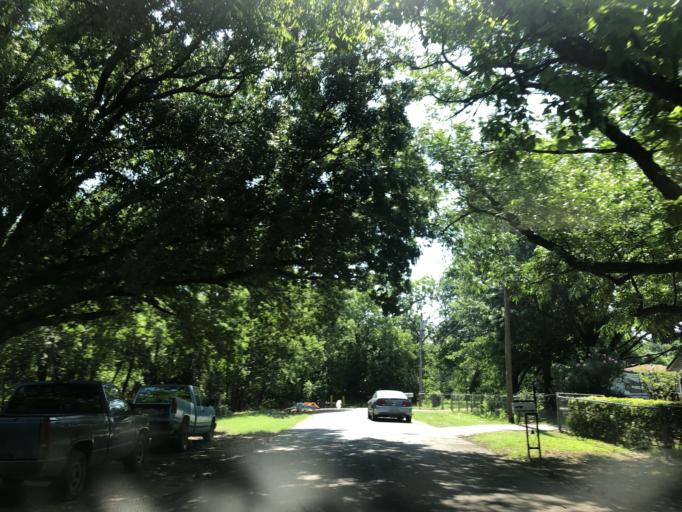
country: US
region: Texas
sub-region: Dallas County
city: Cockrell Hill
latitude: 32.7898
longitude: -96.8716
